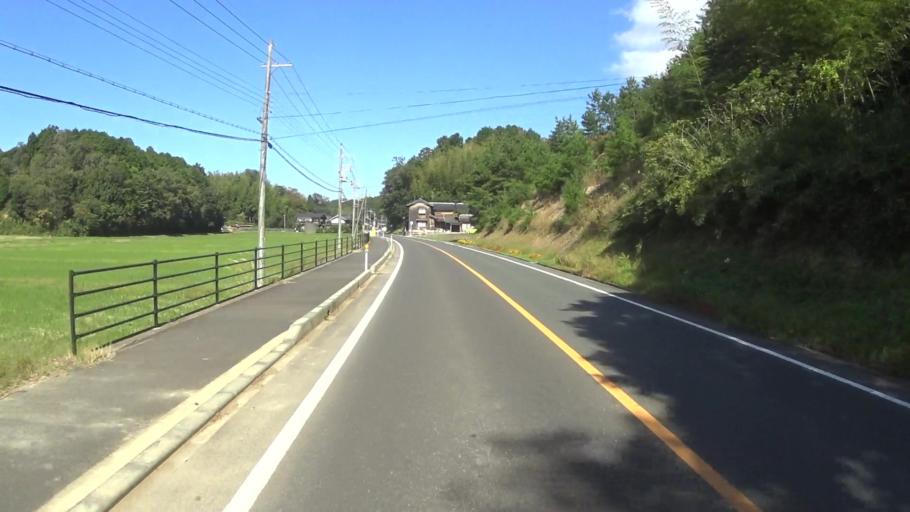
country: JP
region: Kyoto
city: Miyazu
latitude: 35.6506
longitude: 135.0683
